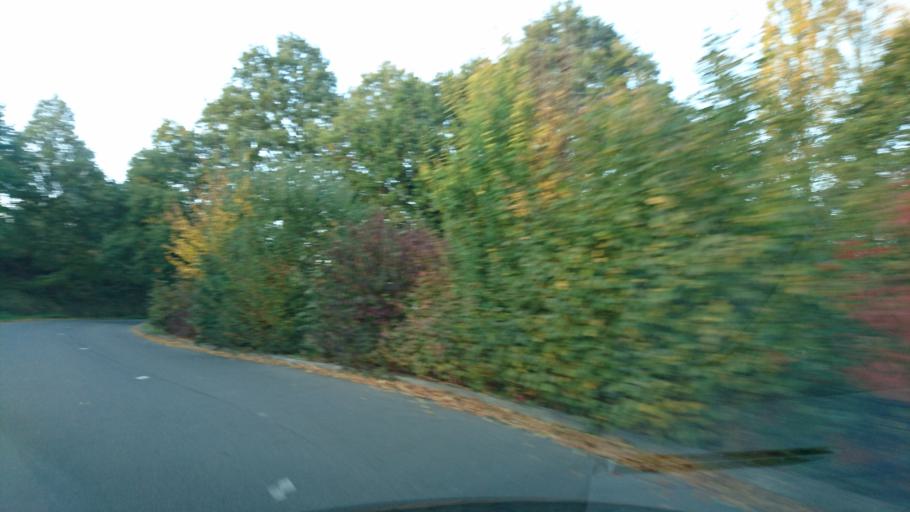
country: FR
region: Brittany
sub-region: Departement d'Ille-et-Vilaine
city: Bruz
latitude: 48.0168
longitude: -1.7564
